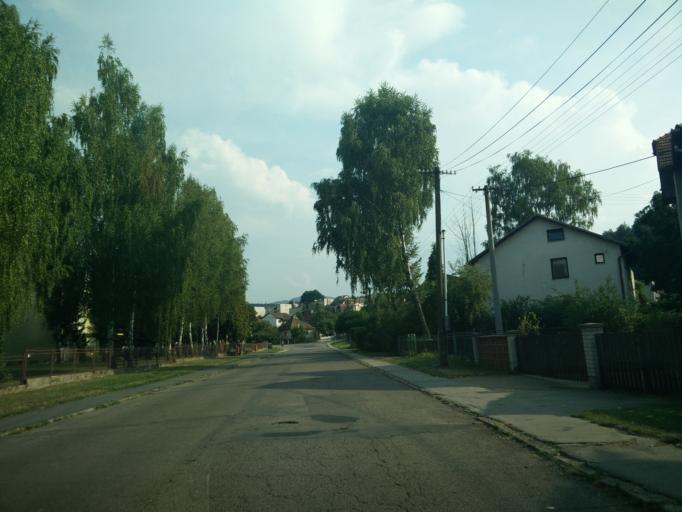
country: SK
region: Banskobystricky
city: Ziar nad Hronom
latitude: 48.5376
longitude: 18.7854
